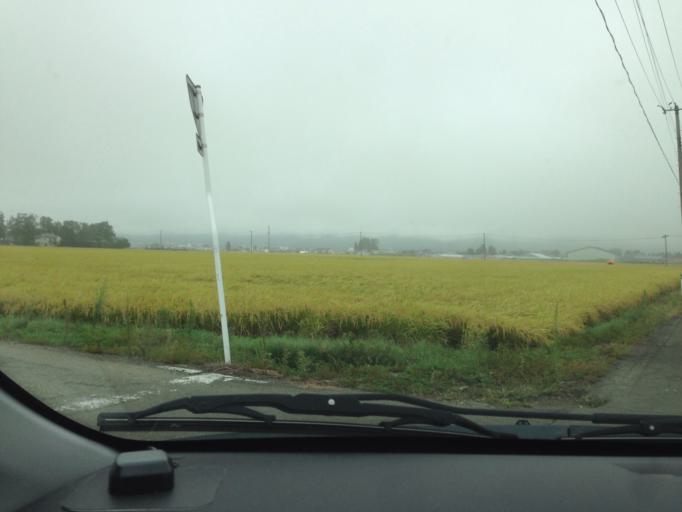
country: JP
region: Fukushima
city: Kitakata
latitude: 37.5732
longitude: 139.8358
